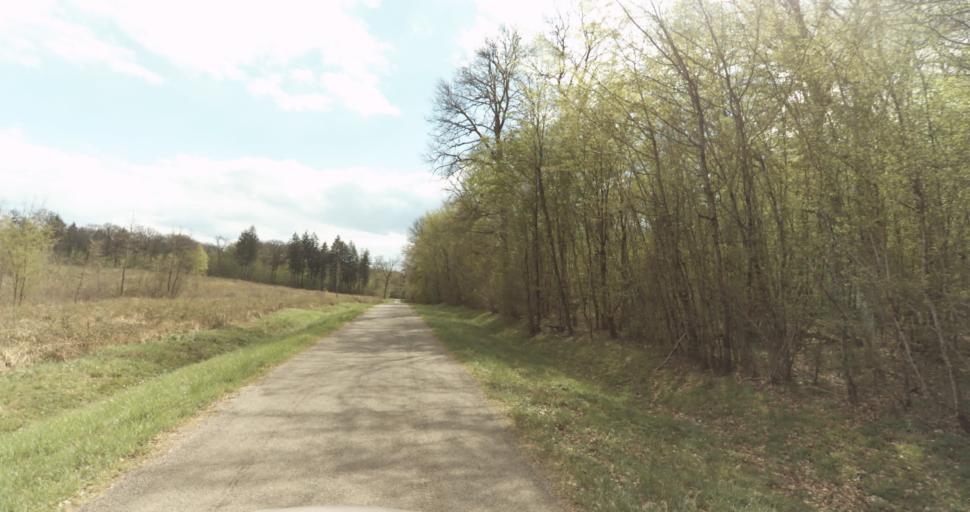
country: FR
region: Bourgogne
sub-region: Departement de la Cote-d'Or
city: Auxonne
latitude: 47.1915
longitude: 5.4520
